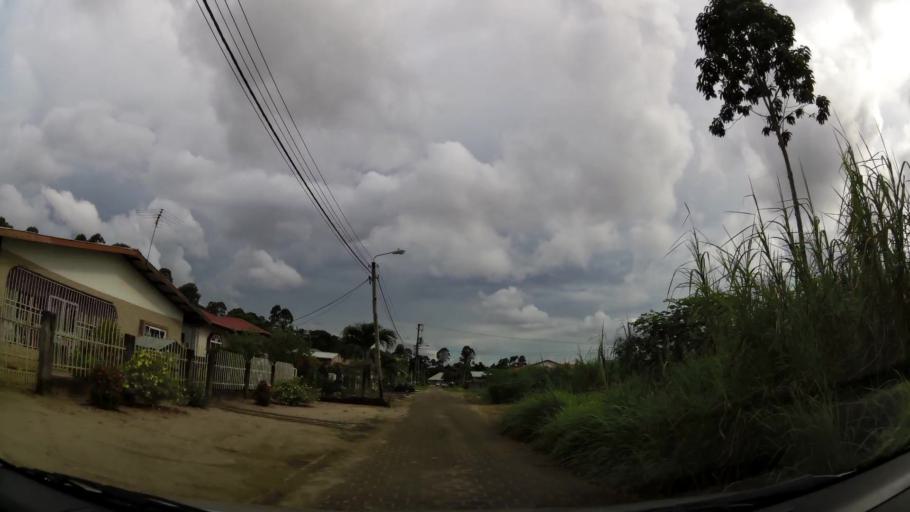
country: SR
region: Paramaribo
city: Paramaribo
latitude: 5.8566
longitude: -55.1775
